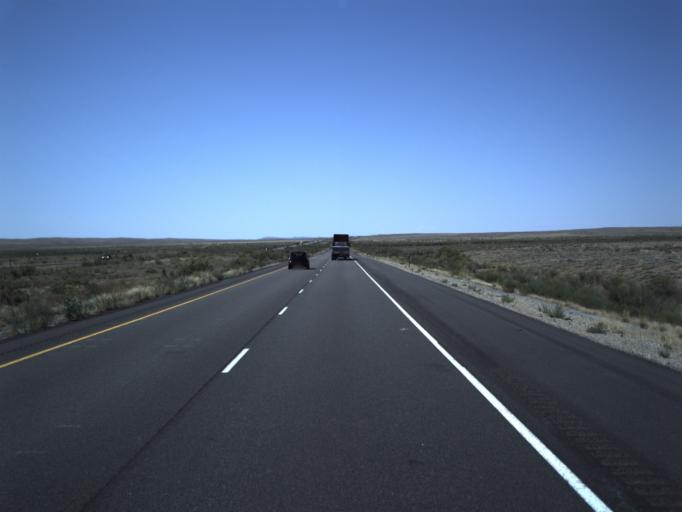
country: US
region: Colorado
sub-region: Mesa County
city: Loma
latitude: 39.0865
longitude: -109.2193
